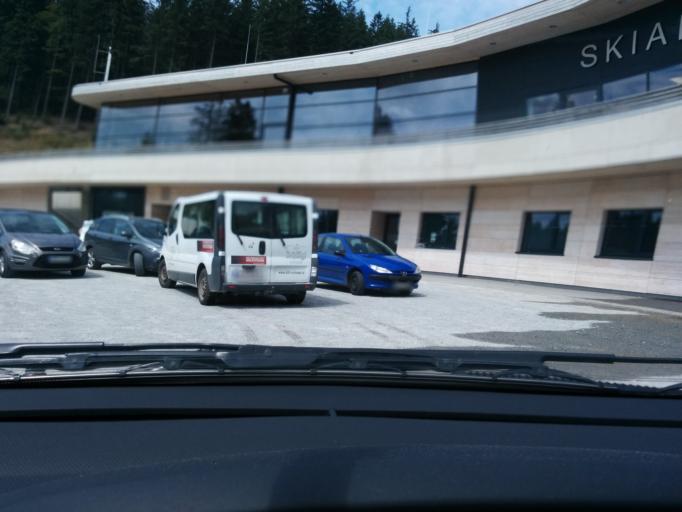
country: AT
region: Upper Austria
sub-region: Politischer Bezirk Rohrbach
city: Ulrichsberg
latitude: 48.7375
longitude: 13.8996
